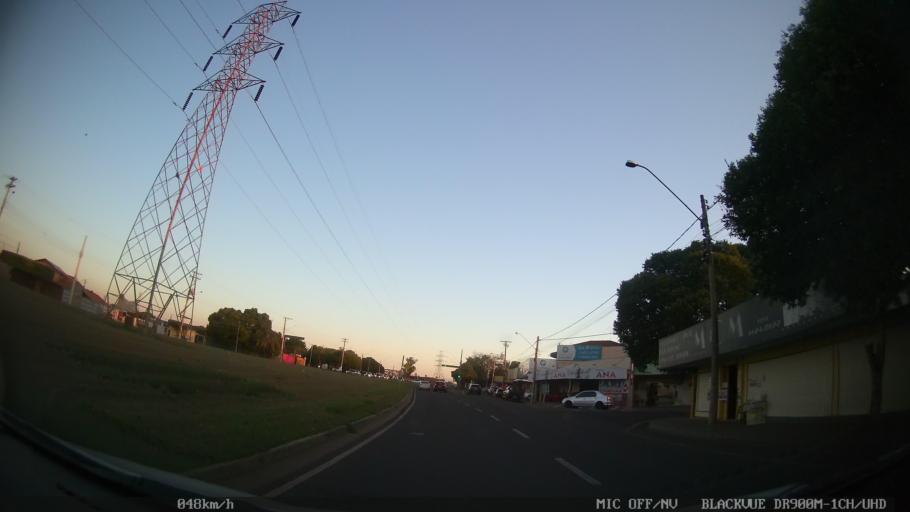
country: BR
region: Sao Paulo
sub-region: Sao Jose Do Rio Preto
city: Sao Jose do Rio Preto
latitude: -20.7928
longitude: -49.3448
